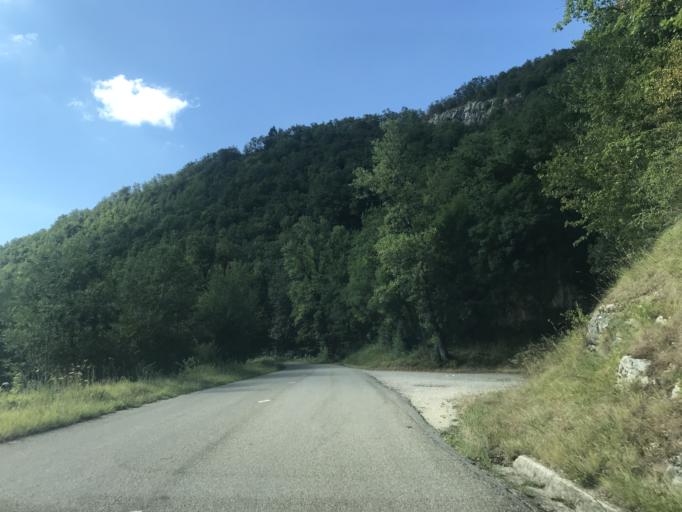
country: FR
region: Rhone-Alpes
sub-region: Departement de la Savoie
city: Brison-Saint-Innocent
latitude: 45.7138
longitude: 5.8268
